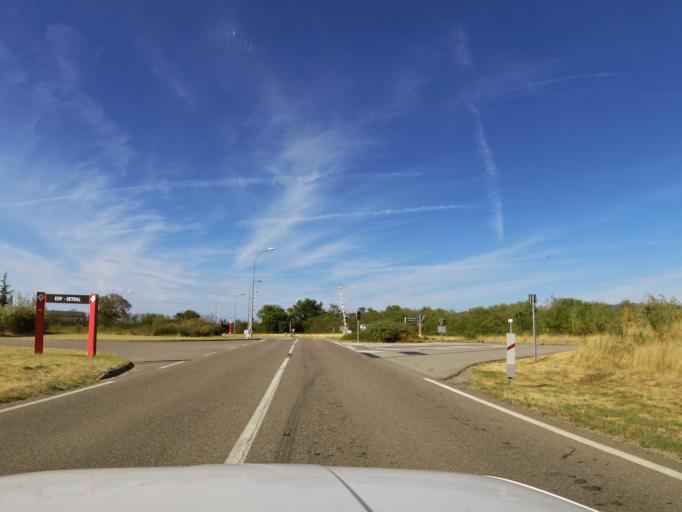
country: FR
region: Rhone-Alpes
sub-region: Departement de l'Isere
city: Hieres-sur-Amby
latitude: 45.8353
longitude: 5.2746
